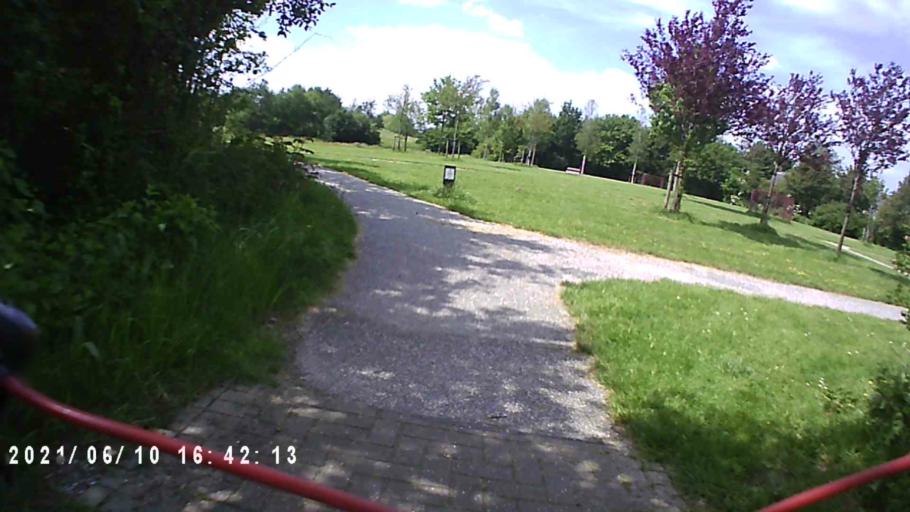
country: NL
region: Friesland
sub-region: Gemeente Achtkarspelen
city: Buitenpost
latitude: 53.2461
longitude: 6.1358
